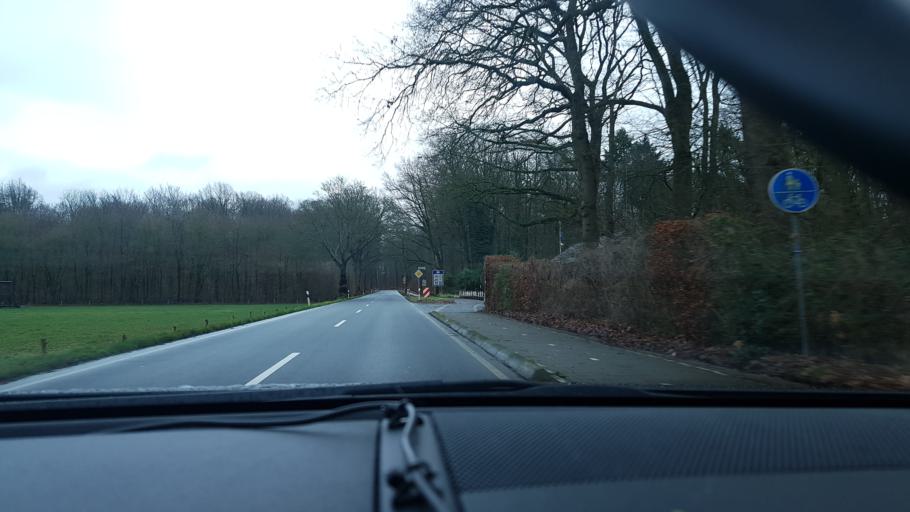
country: NL
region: Limburg
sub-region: Gemeente Beesel
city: Offenbeek
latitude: 51.2307
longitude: 6.0809
